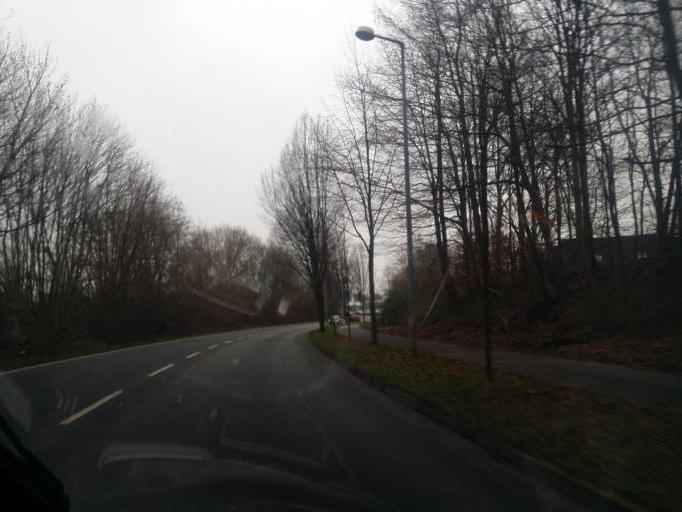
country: DE
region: Schleswig-Holstein
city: Heide
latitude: 54.2011
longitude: 9.1240
